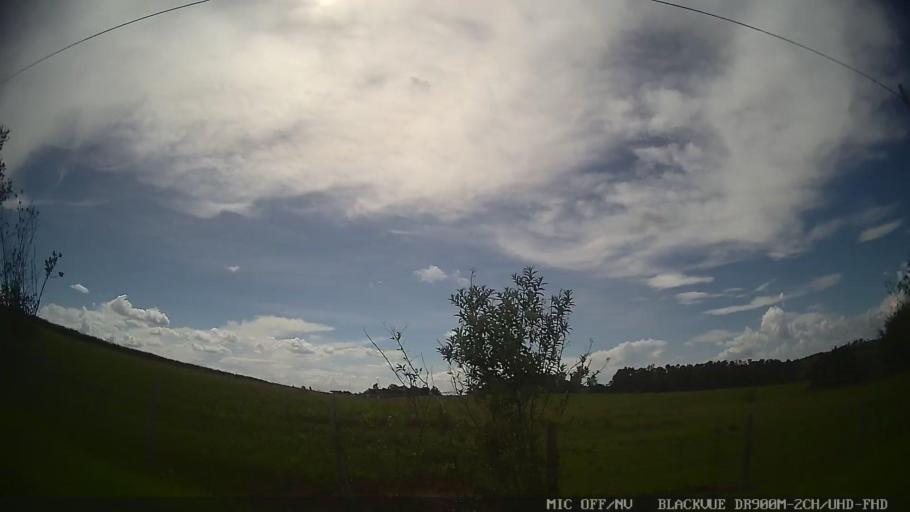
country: BR
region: Sao Paulo
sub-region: Conchas
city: Conchas
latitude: -22.9688
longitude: -47.9845
